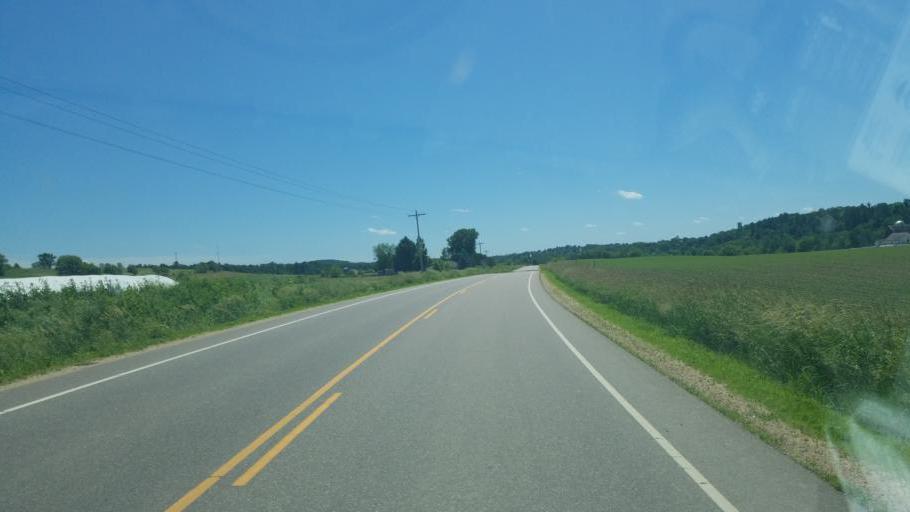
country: US
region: Wisconsin
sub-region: Juneau County
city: Elroy
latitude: 43.7707
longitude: -90.2716
